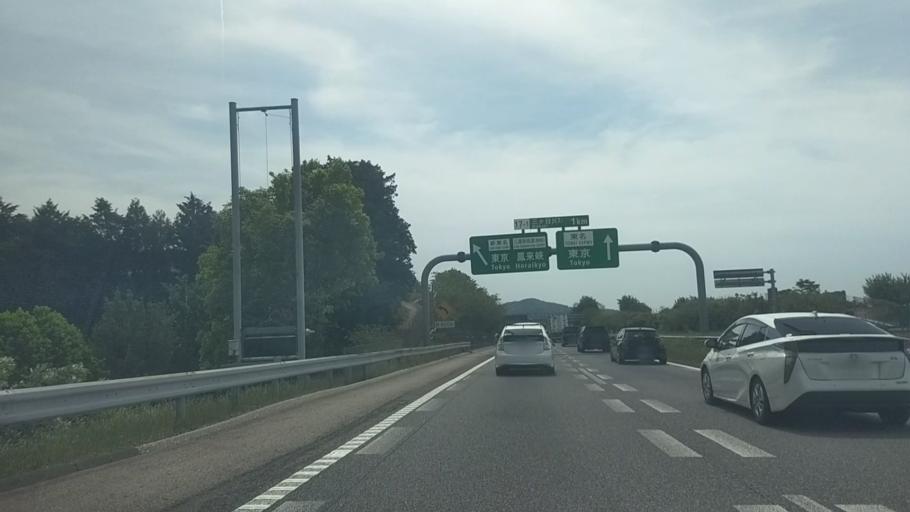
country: JP
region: Aichi
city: Shinshiro
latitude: 34.8354
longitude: 137.5323
